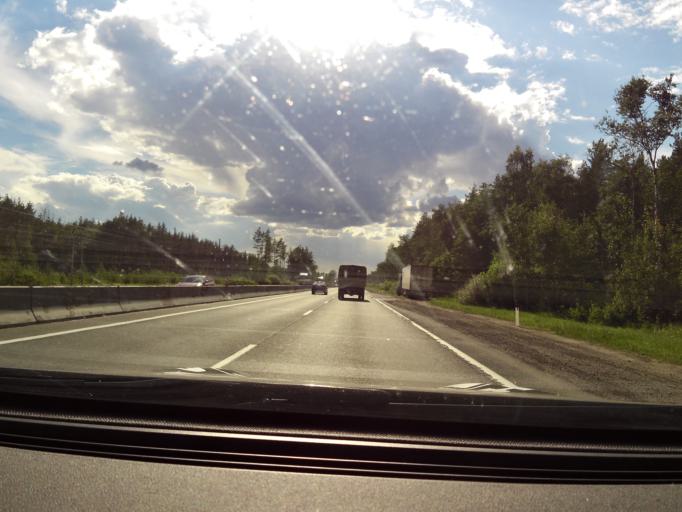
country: RU
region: Nizjnij Novgorod
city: Pyra
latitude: 56.2915
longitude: 43.3116
